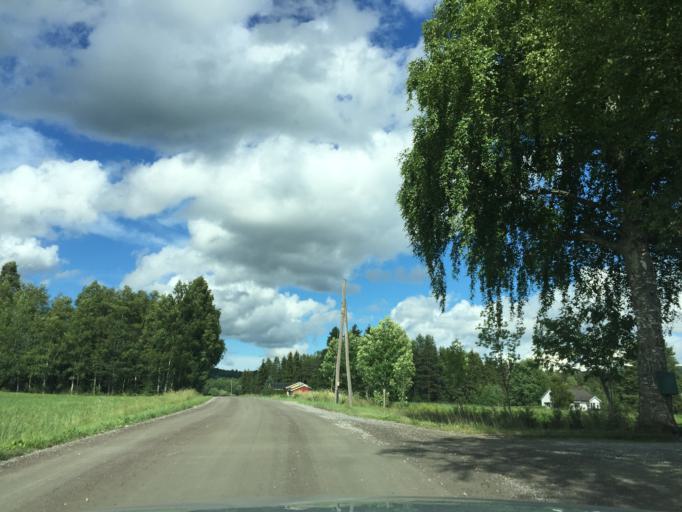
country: NO
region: Hedmark
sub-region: Kongsvinger
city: Spetalen
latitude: 60.2400
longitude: 11.8332
